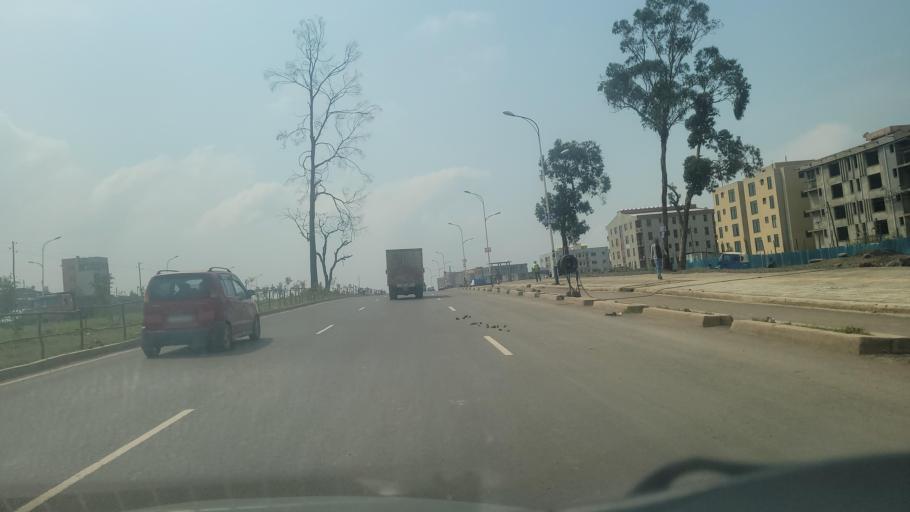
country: ET
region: Adis Abeba
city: Addis Ababa
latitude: 8.9405
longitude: 38.7229
